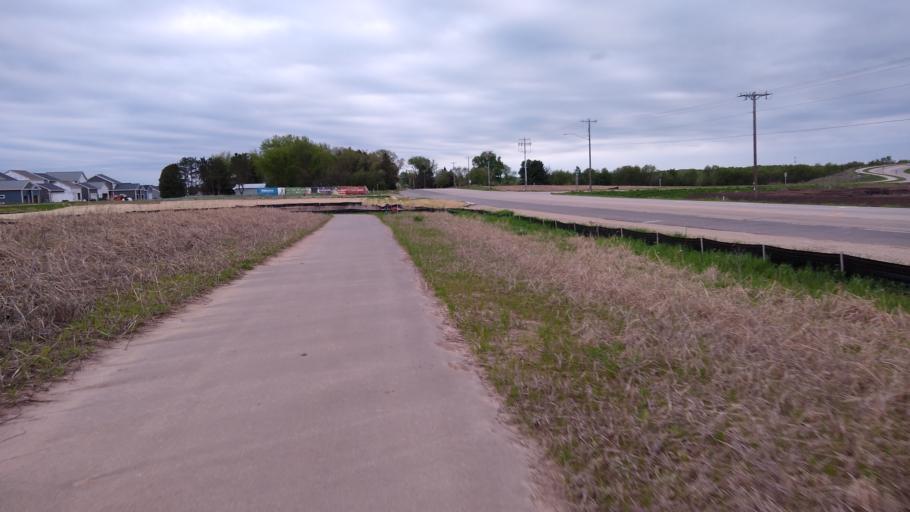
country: US
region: Wisconsin
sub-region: Dane County
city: Monona
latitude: 43.0128
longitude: -89.3755
